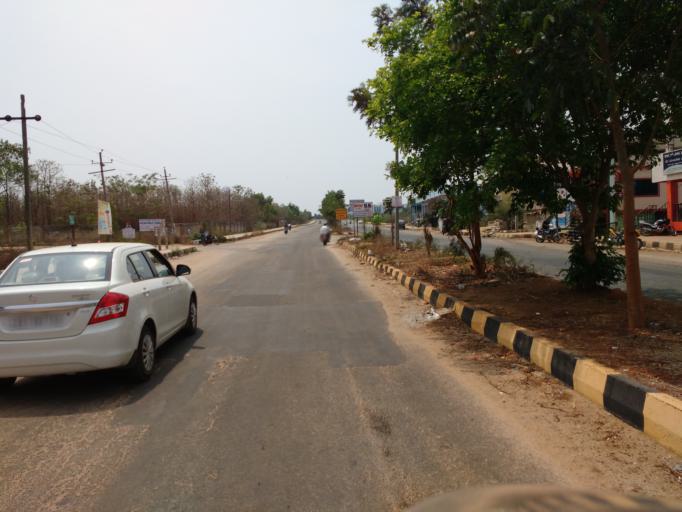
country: IN
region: Karnataka
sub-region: Hassan
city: Hassan
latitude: 13.0162
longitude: 76.1175
